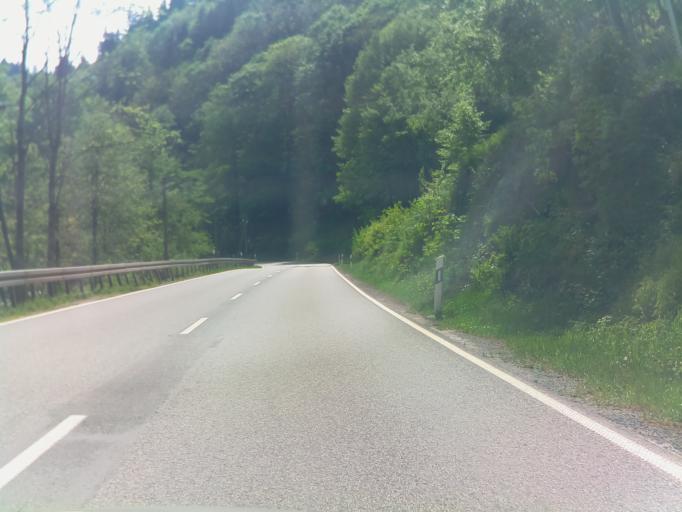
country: DE
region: Thuringia
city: Ilfeld
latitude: 51.6177
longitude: 10.8014
